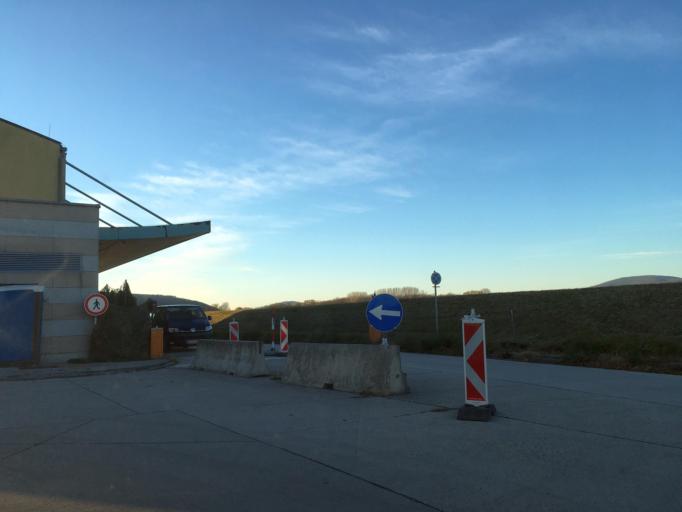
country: AT
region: Burgenland
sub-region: Politischer Bezirk Neusiedl am See
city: Kittsee
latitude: 48.1222
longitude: 17.0590
